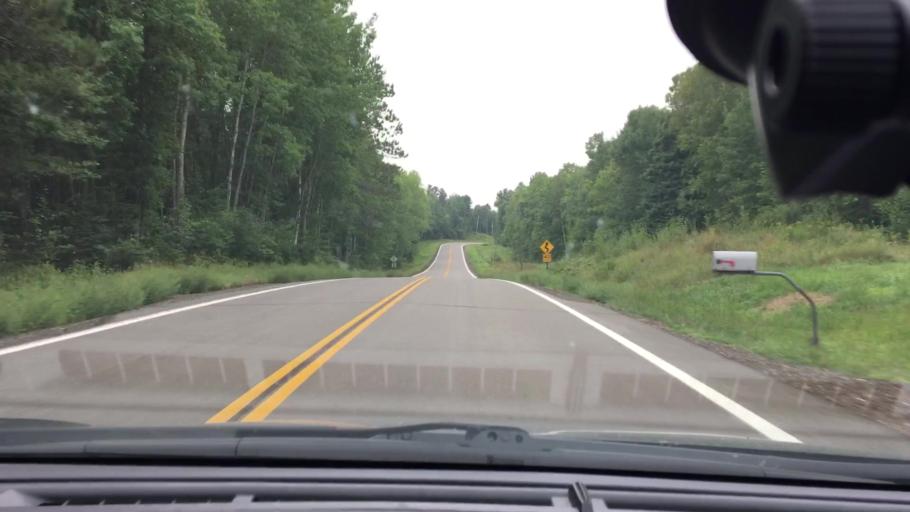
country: US
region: Minnesota
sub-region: Crow Wing County
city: Cross Lake
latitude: 46.6576
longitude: -93.9761
